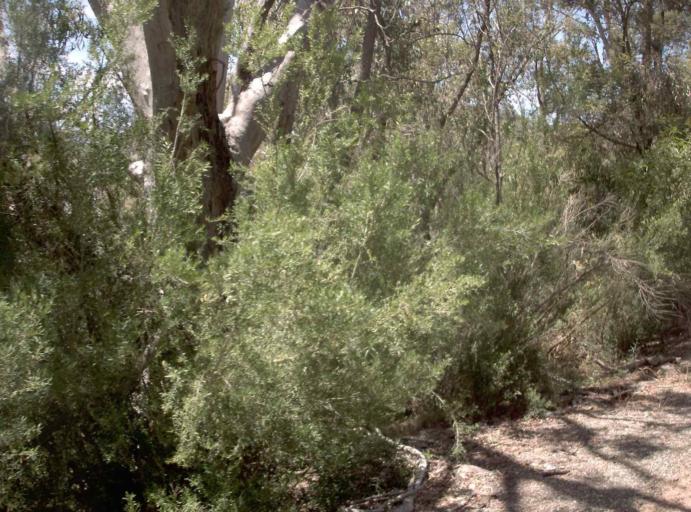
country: AU
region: Victoria
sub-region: East Gippsland
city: Bairnsdale
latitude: -37.4184
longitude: 147.8326
